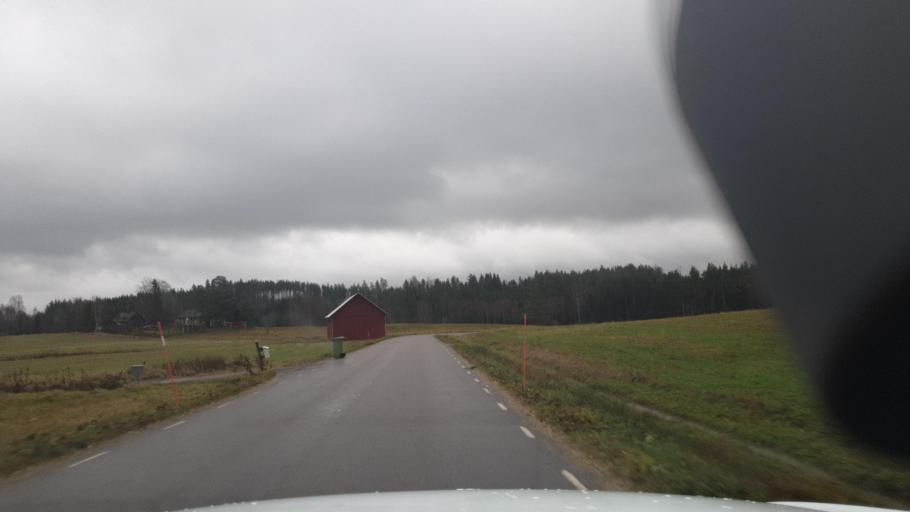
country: SE
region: Vaermland
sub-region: Eda Kommun
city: Charlottenberg
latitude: 59.8147
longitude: 12.1598
